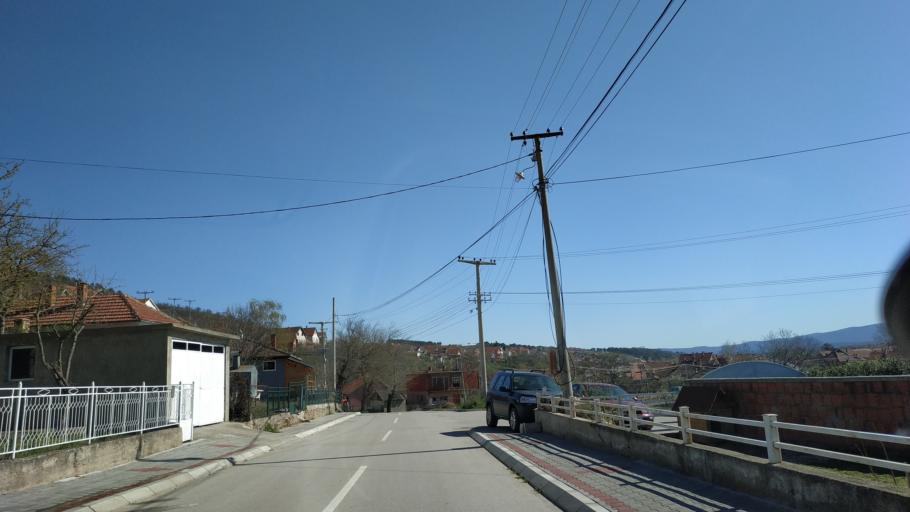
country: RS
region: Central Serbia
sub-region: Nisavski Okrug
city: Aleksinac
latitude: 43.5473
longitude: 21.7132
